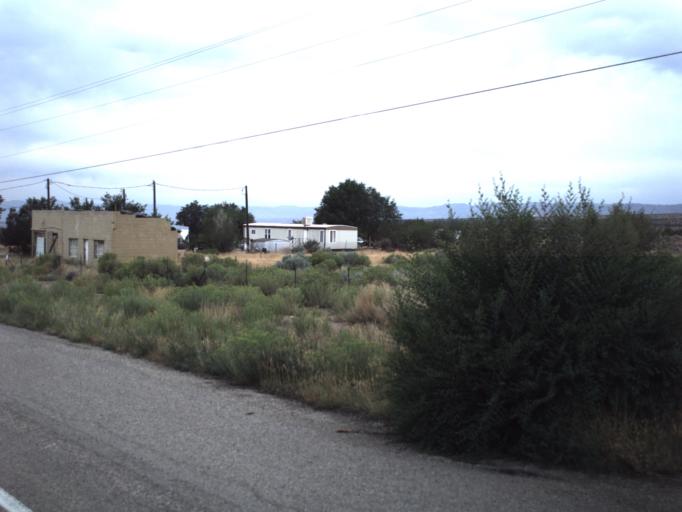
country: US
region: Utah
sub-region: Carbon County
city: East Carbon City
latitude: 39.5407
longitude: -110.4295
